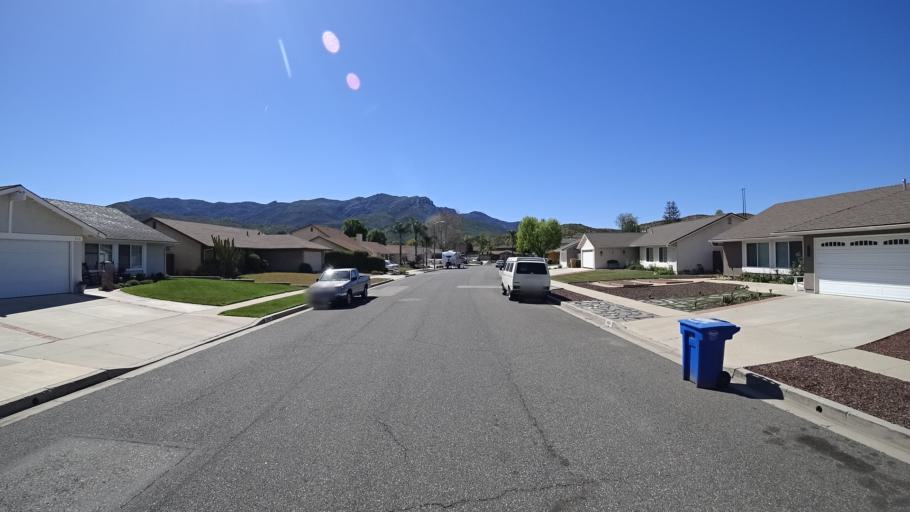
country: US
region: California
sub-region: Ventura County
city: Casa Conejo
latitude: 34.1586
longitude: -118.9636
